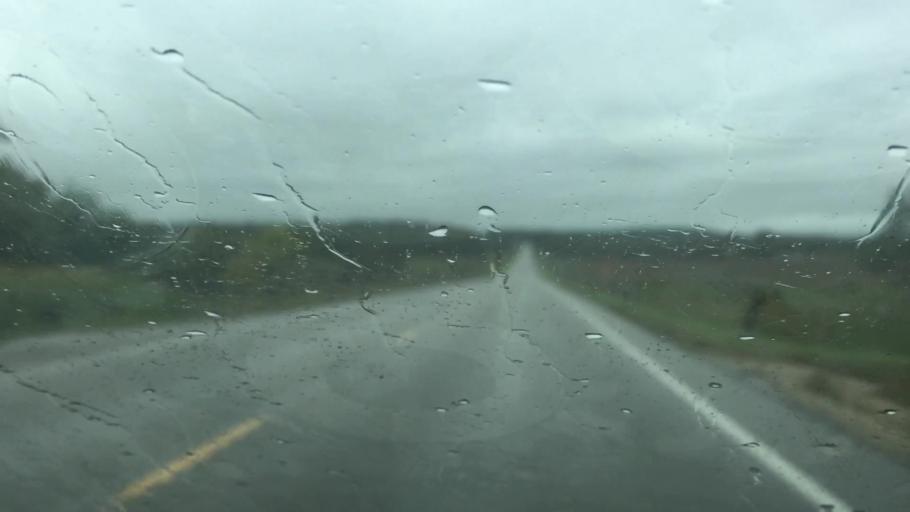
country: US
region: Kansas
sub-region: Anderson County
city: Garnett
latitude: 38.3809
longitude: -95.1123
